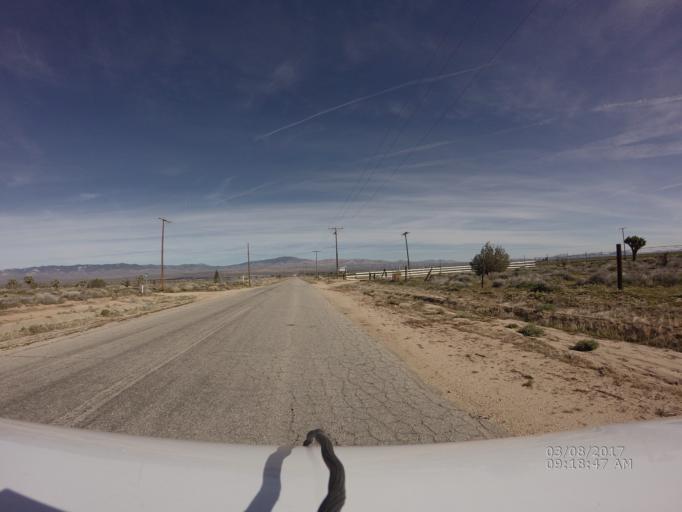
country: US
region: California
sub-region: Los Angeles County
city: Green Valley
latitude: 34.7888
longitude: -118.4666
